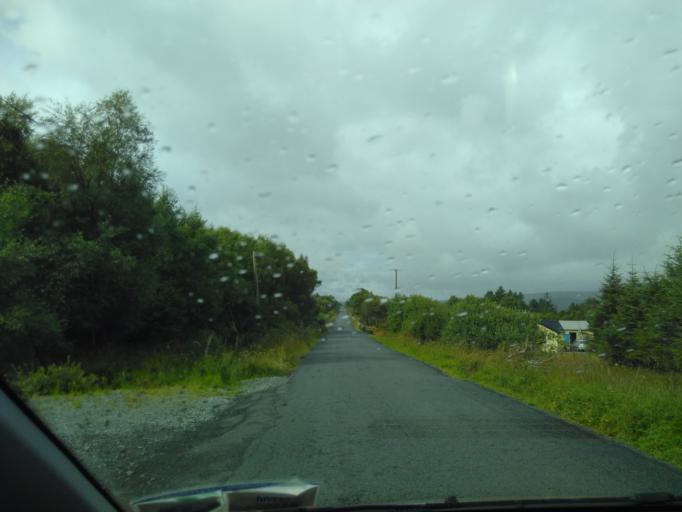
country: IE
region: Ulster
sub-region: County Donegal
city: Dunlewy
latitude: 54.9766
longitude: -7.9341
